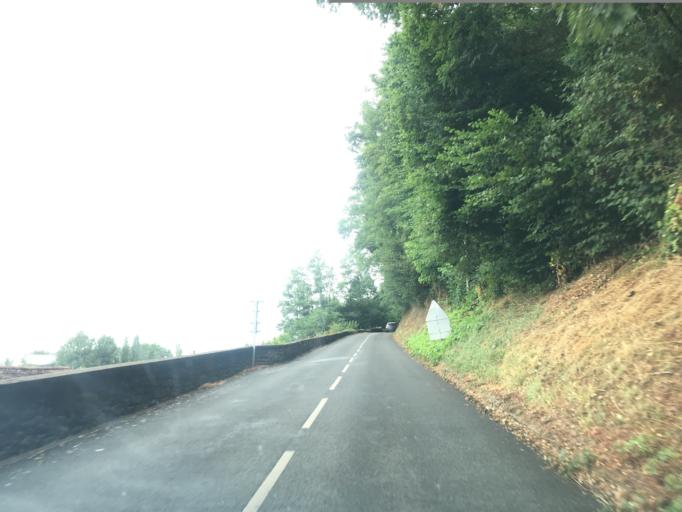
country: FR
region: Aquitaine
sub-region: Departement de la Dordogne
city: Cenac-et-Saint-Julien
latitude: 44.8024
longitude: 1.2047
